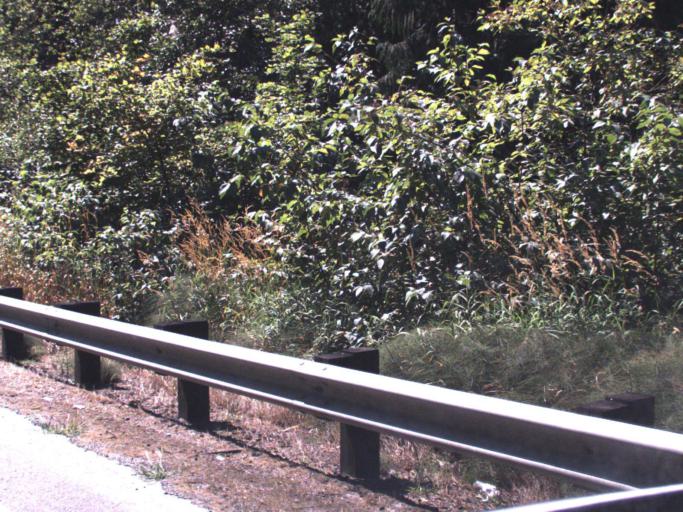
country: US
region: Washington
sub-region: King County
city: Ames Lake
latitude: 47.5951
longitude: -121.9603
